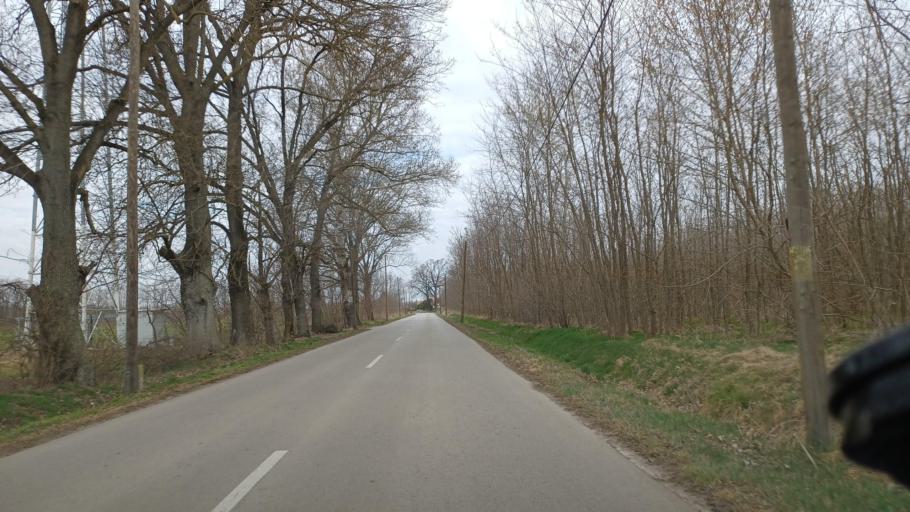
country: HU
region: Tolna
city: Tengelic
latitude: 46.5418
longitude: 18.7031
